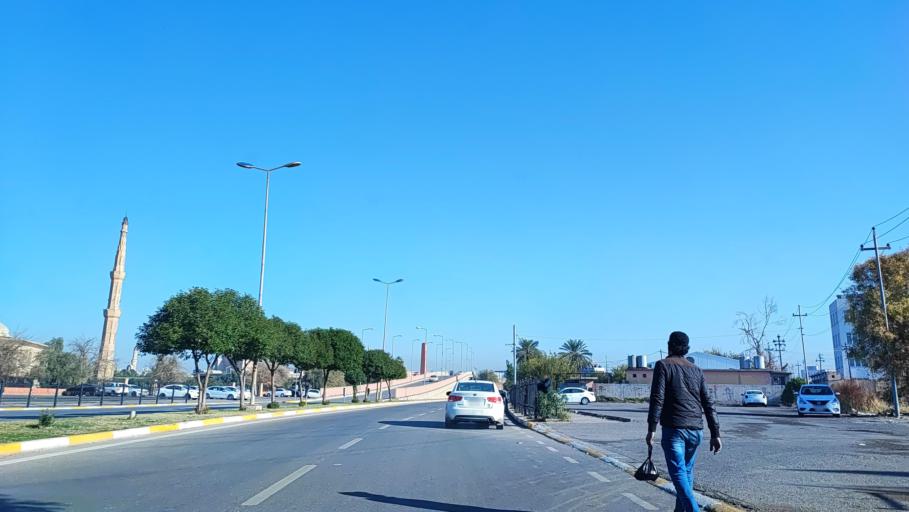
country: IQ
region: Arbil
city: Erbil
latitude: 36.1819
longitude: 44.0043
